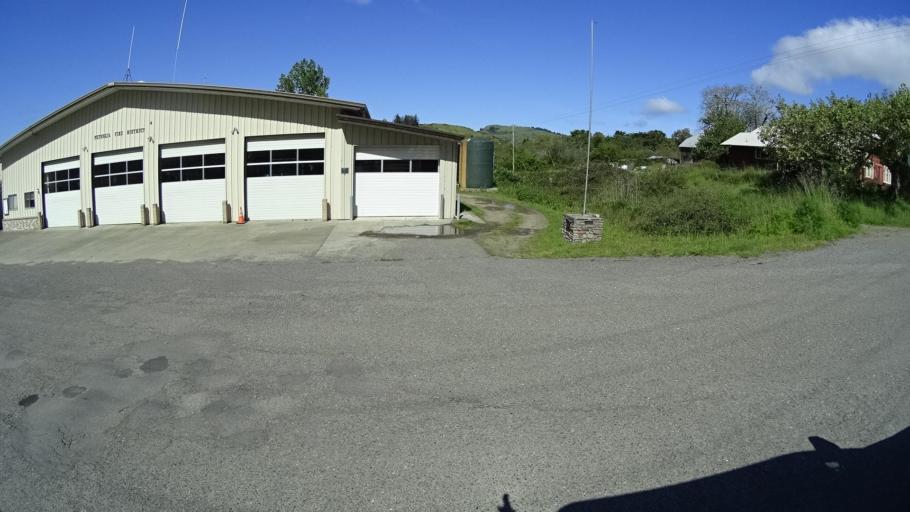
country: US
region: California
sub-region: Humboldt County
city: Rio Dell
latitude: 40.3251
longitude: -124.2872
